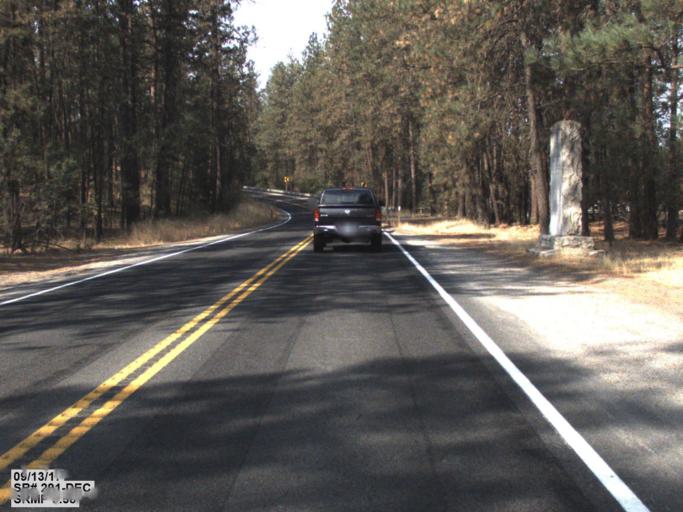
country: US
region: Washington
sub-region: Spokane County
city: Fairwood
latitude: 47.7804
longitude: -117.5393
